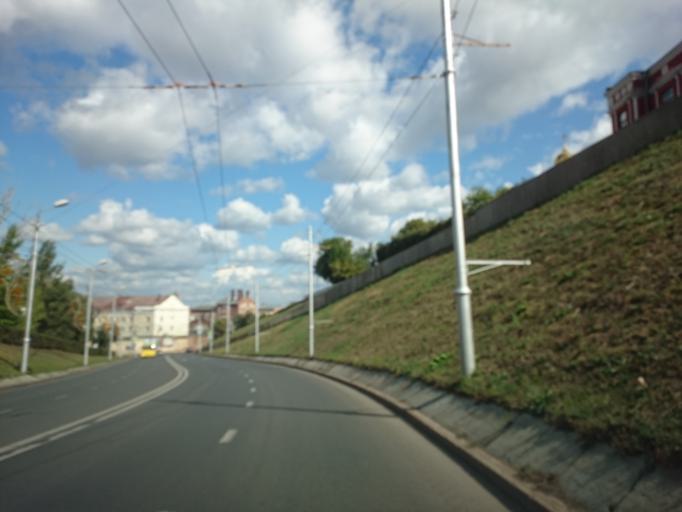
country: RU
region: Samara
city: Samara
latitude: 53.1978
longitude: 50.0968
